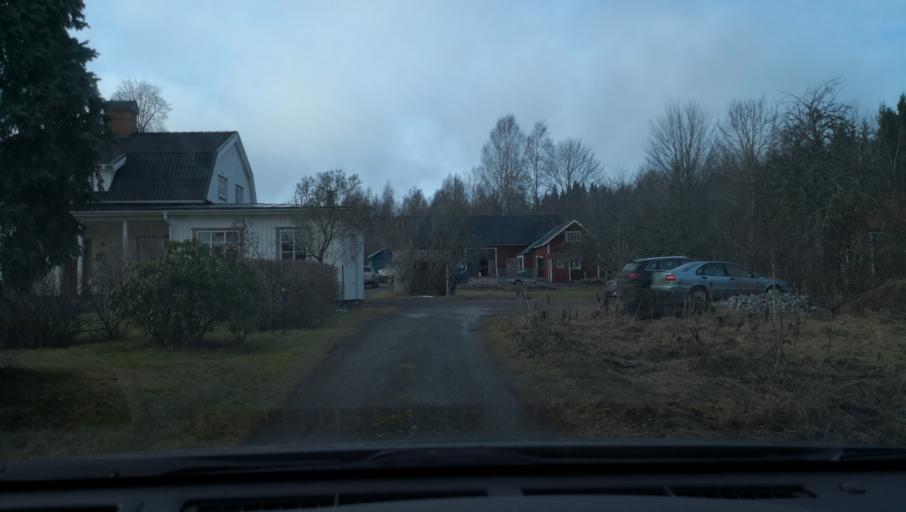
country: SE
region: Vaestra Goetaland
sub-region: Gullspangs Kommun
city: Gullspang
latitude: 58.9628
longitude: 14.0943
